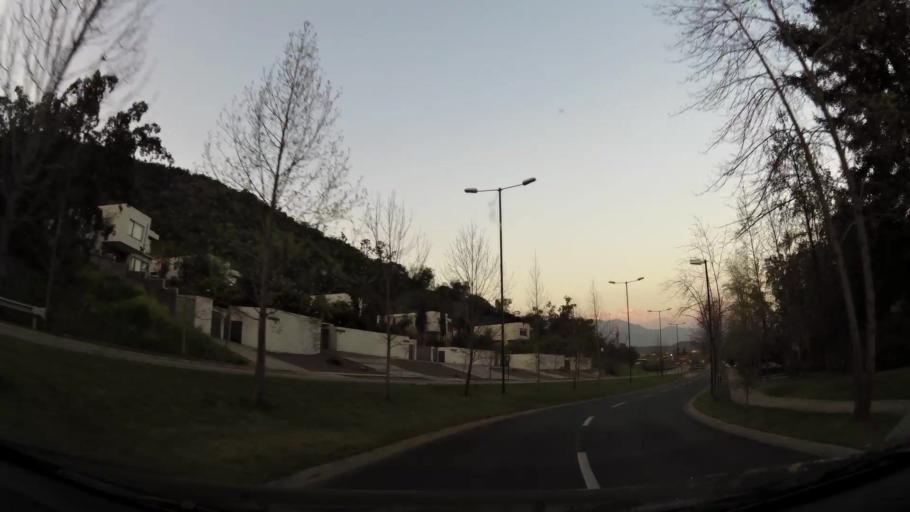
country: CL
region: Santiago Metropolitan
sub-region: Provincia de Chacabuco
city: Chicureo Abajo
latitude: -33.3319
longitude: -70.5528
